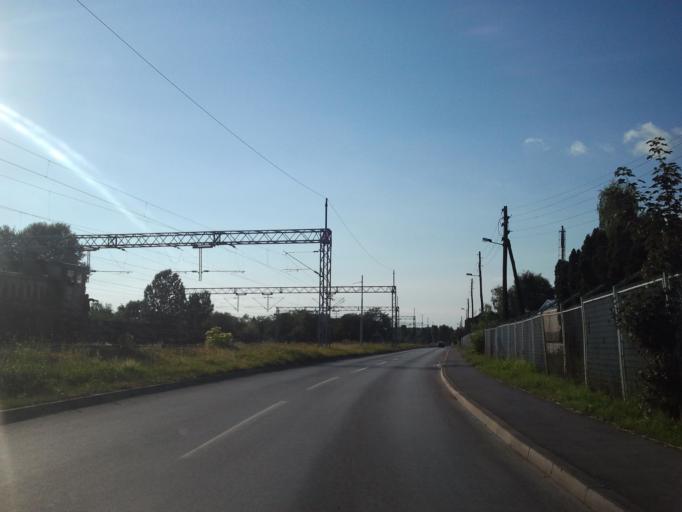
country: HR
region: Sisacko-Moslavacka
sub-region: Grad Sisak
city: Sisak
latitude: 45.4589
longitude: 16.3902
